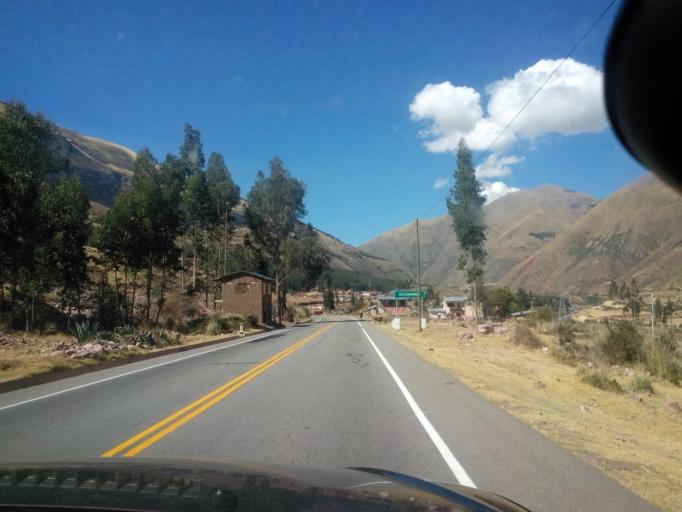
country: PE
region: Cusco
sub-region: Provincia de Quispicanchis
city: Cusipata
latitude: -13.9550
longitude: -71.4998
